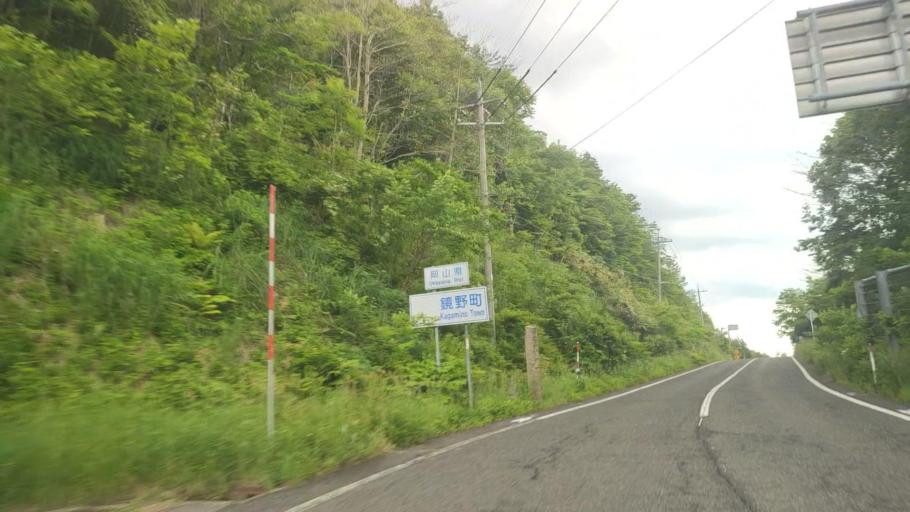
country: JP
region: Tottori
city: Kurayoshi
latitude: 35.3128
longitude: 134.0037
